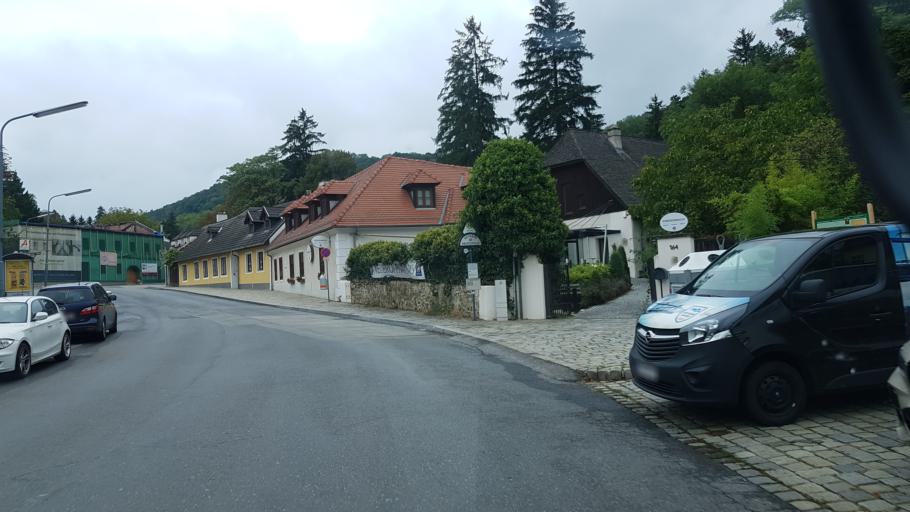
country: AT
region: Lower Austria
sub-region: Politischer Bezirk Wien-Umgebung
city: Klosterneuburg
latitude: 48.2539
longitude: 16.3178
